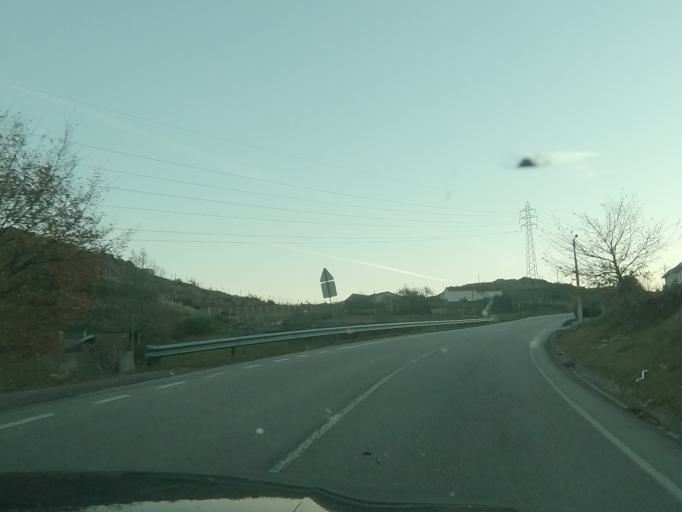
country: PT
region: Vila Real
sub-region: Vila Pouca de Aguiar
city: Vila Pouca de Aguiar
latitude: 41.4124
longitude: -7.6874
